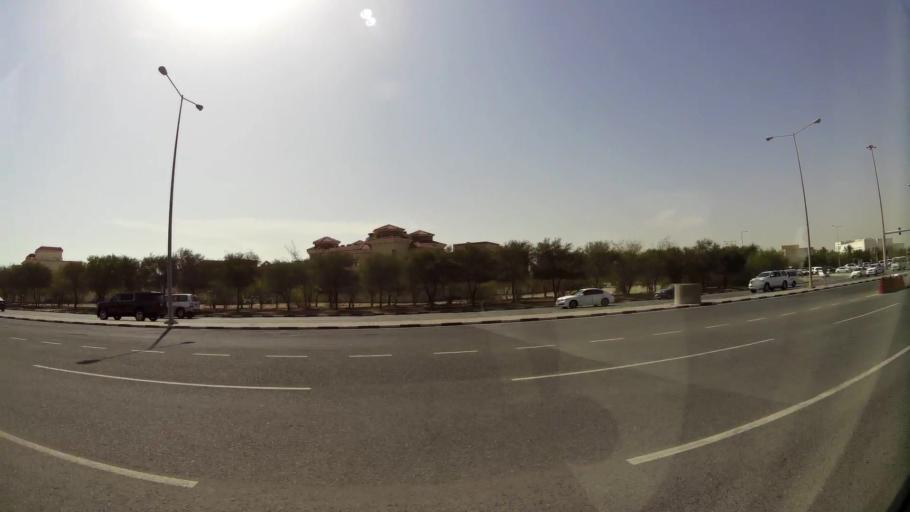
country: QA
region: Baladiyat ad Dawhah
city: Doha
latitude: 25.3511
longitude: 51.5018
